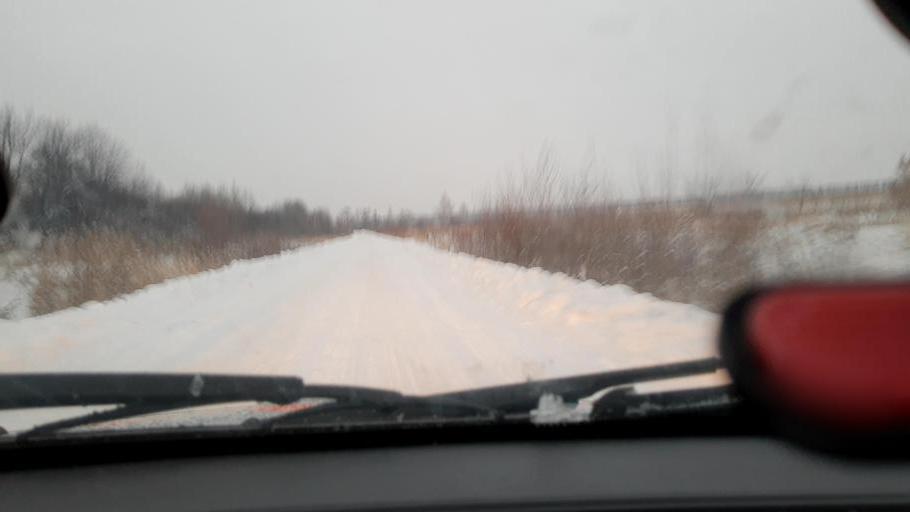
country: RU
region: Bashkortostan
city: Iglino
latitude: 54.7362
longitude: 56.2414
